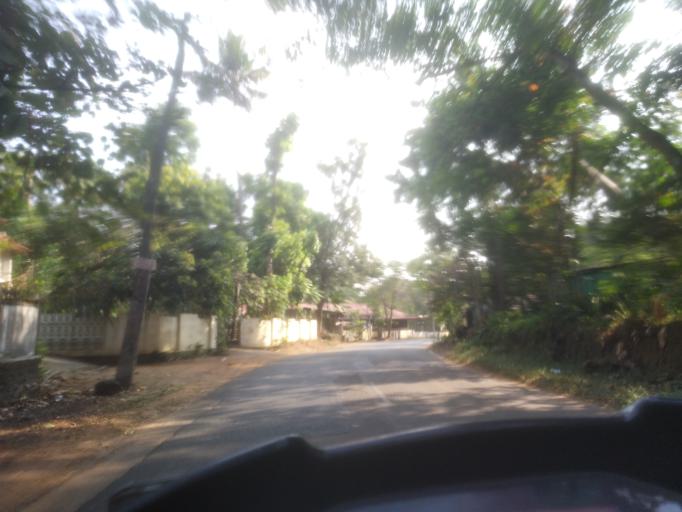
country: IN
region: Kerala
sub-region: Ernakulam
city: Piravam
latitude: 9.8355
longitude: 76.5209
